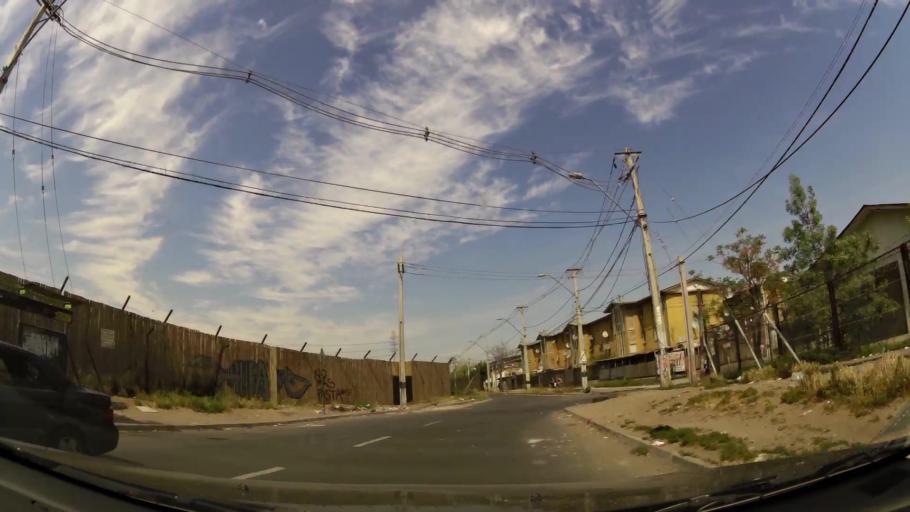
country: CL
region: Santiago Metropolitan
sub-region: Provincia de Cordillera
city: Puente Alto
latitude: -33.5914
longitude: -70.6006
